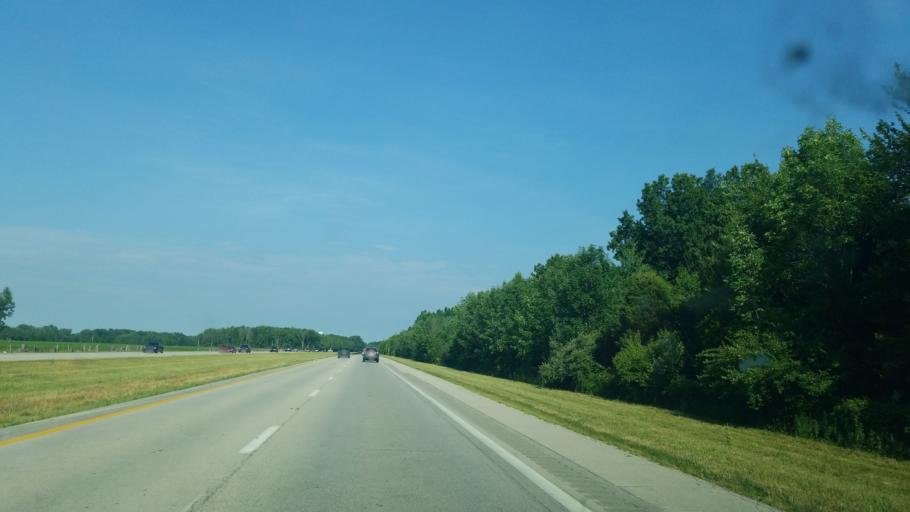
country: US
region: Ohio
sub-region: Clermont County
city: Williamsburg
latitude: 39.0608
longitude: -84.0106
